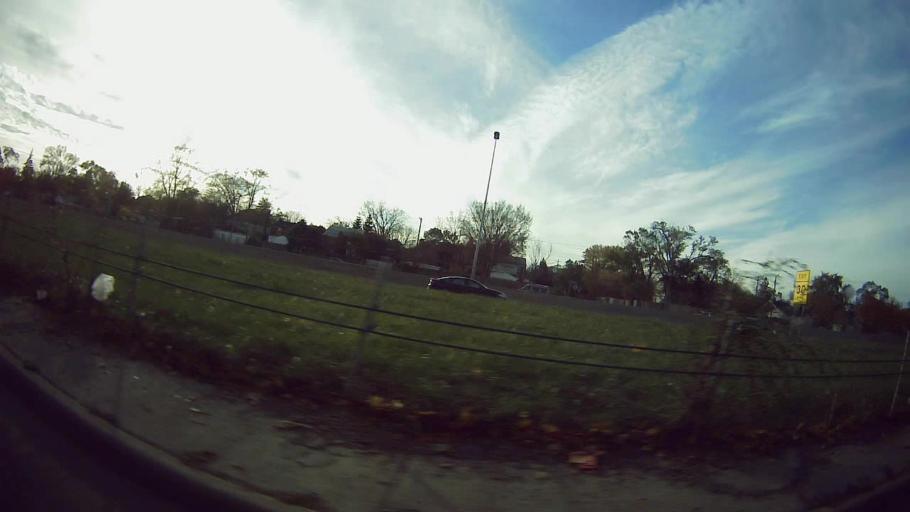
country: US
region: Michigan
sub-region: Oakland County
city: Oak Park
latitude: 42.4117
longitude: -83.2184
